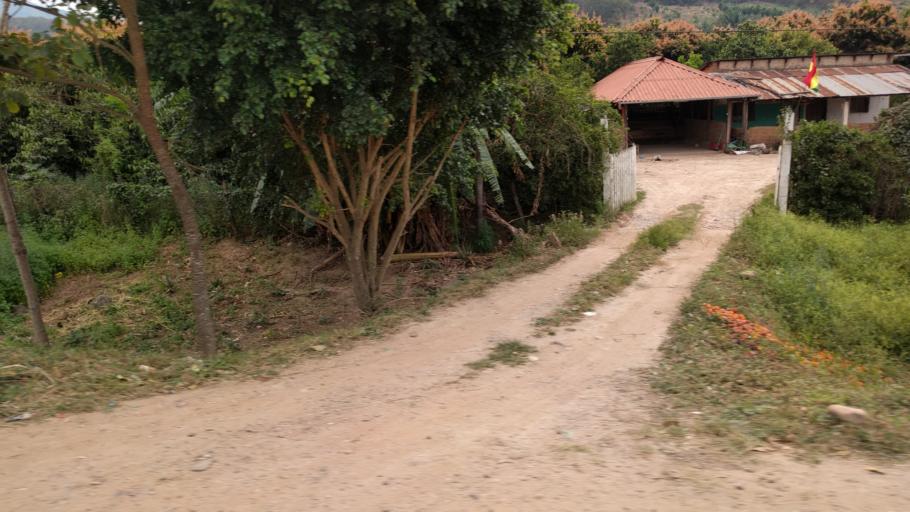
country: BO
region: Santa Cruz
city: Jorochito
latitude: -18.1570
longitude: -63.4999
